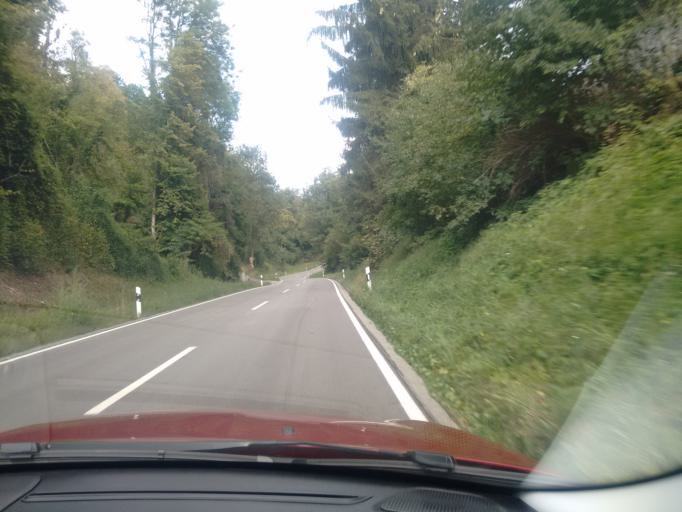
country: DE
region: Bavaria
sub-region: Upper Bavaria
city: Burghausen
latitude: 48.1500
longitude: 12.8006
